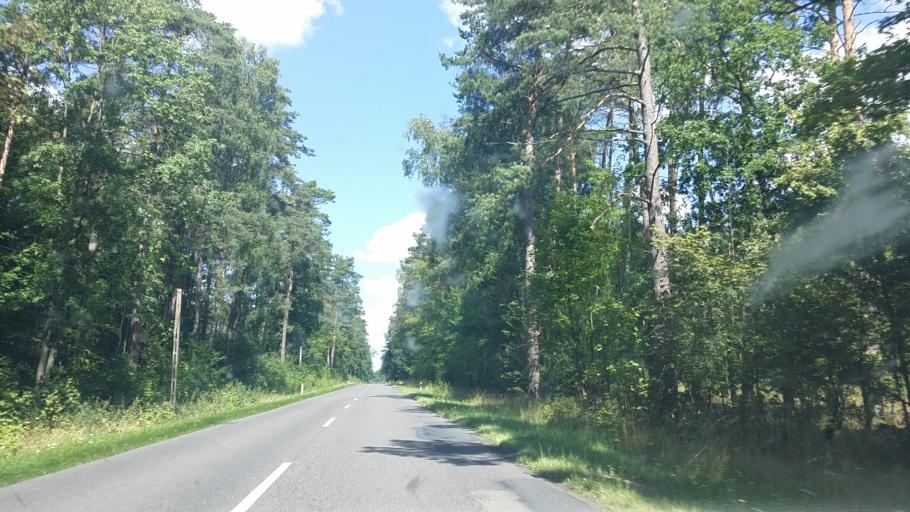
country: PL
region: West Pomeranian Voivodeship
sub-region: Powiat swidwinski
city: Slawoborze
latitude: 53.9409
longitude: 15.6751
